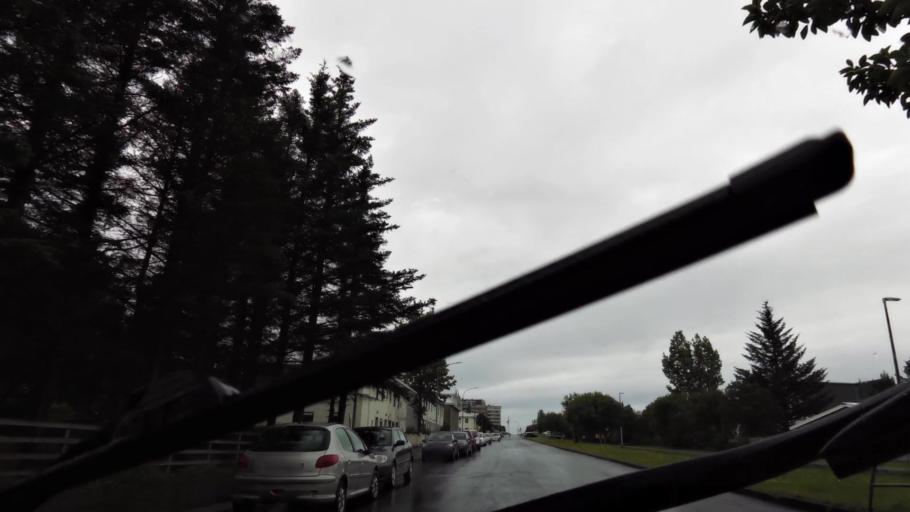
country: IS
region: Capital Region
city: Reykjavik
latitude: 64.1239
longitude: -21.8734
